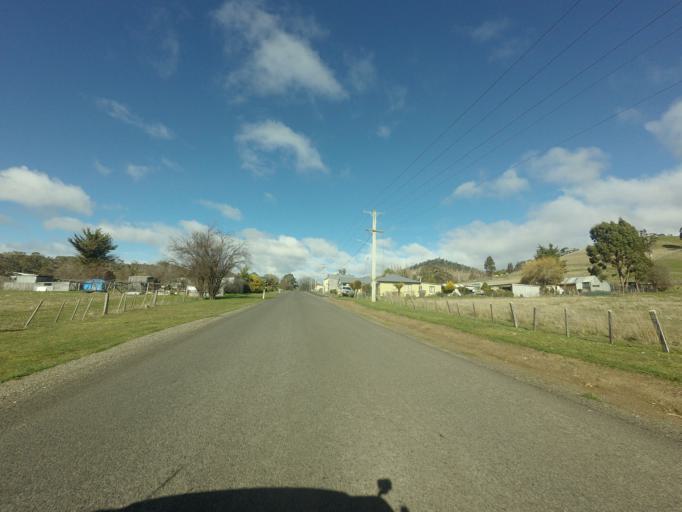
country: AU
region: Tasmania
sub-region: Derwent Valley
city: New Norfolk
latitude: -42.6132
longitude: 146.7133
